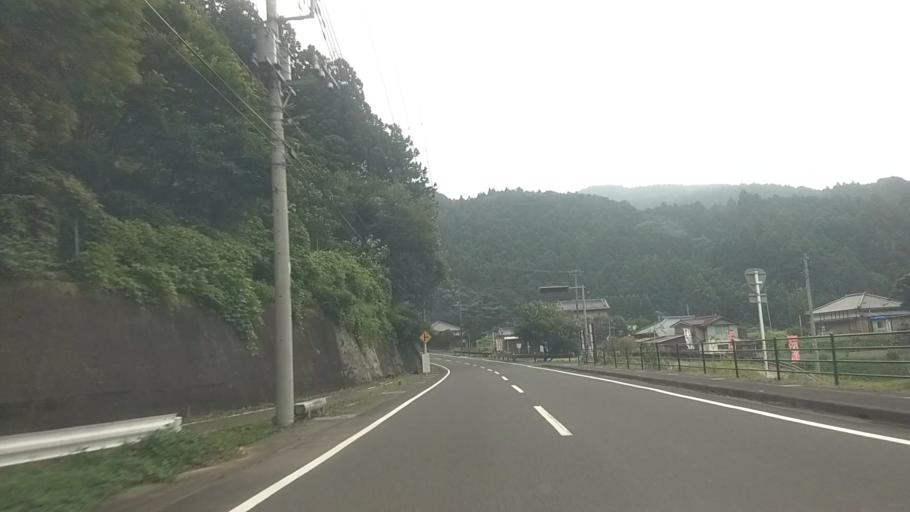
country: JP
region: Chiba
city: Kawaguchi
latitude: 35.2194
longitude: 140.1366
